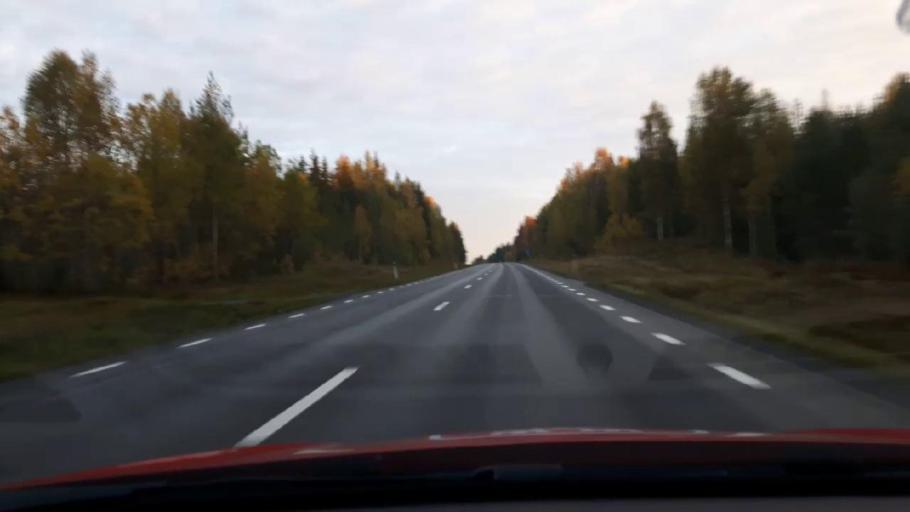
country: SE
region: Jaemtland
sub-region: OEstersunds Kommun
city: Lit
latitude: 63.3037
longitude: 14.8701
